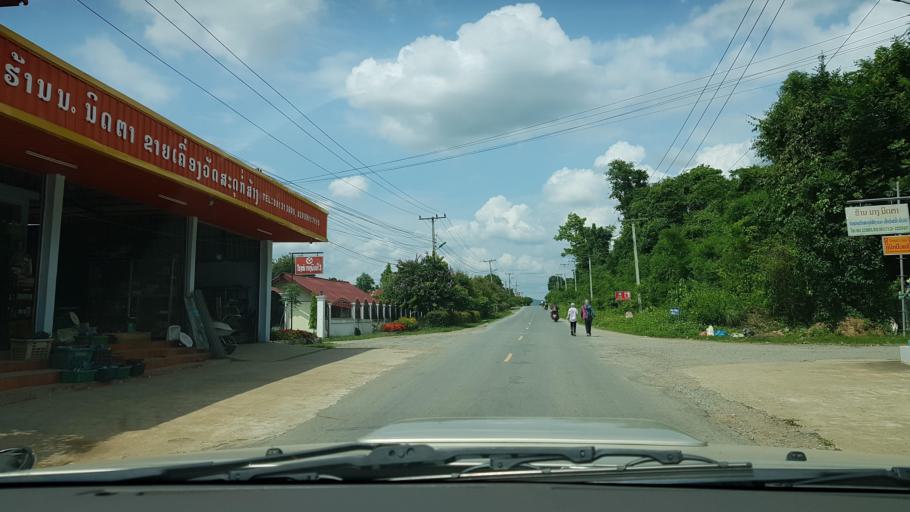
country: LA
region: Loungnamtha
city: Muang Nale
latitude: 20.1275
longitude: 101.4392
